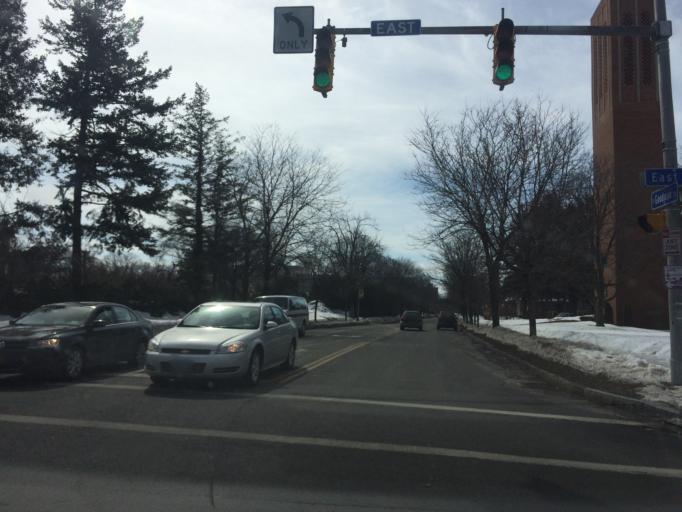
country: US
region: New York
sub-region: Monroe County
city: Rochester
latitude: 43.1535
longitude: -77.5882
